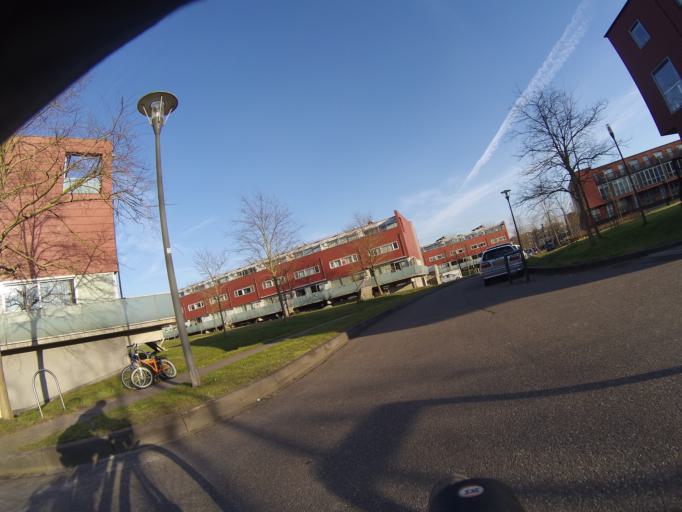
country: NL
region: Utrecht
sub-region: Gemeente Amersfoort
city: Hoogland
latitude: 52.2046
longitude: 5.3669
